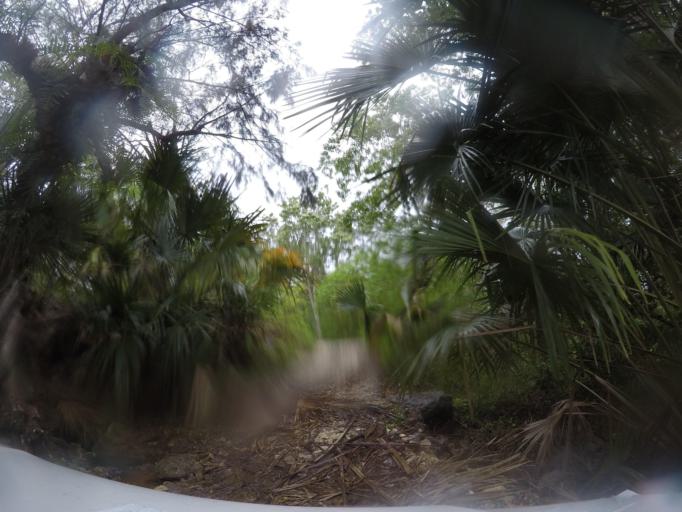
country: TL
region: Baucau
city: Venilale
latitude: -8.6433
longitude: 126.4347
